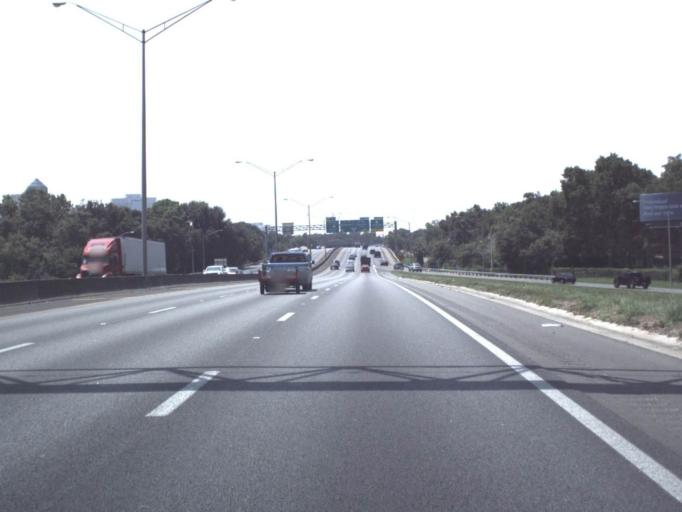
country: US
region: Florida
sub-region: Duval County
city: Jacksonville
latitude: 30.3471
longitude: -81.6684
